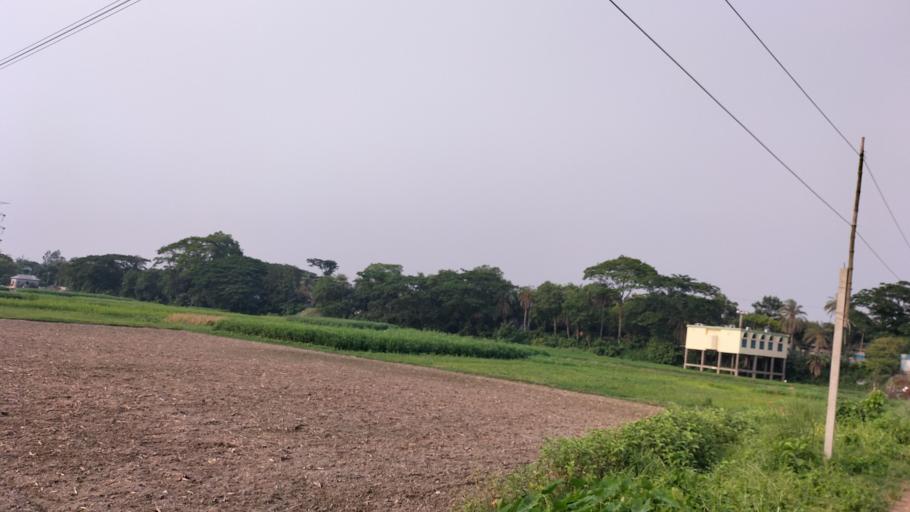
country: BD
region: Dhaka
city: Azimpur
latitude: 23.6688
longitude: 90.3207
